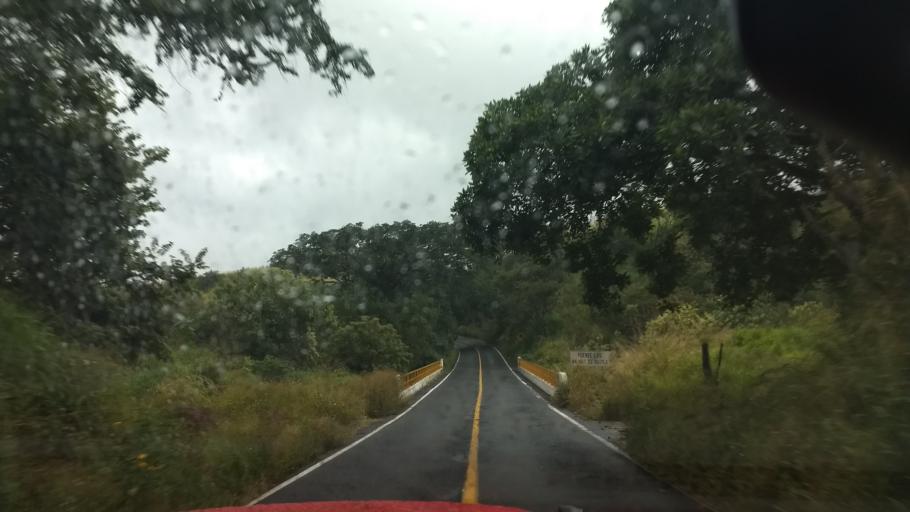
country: MX
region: Jalisco
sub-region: Tonila
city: San Marcos
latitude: 19.4366
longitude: -103.4941
